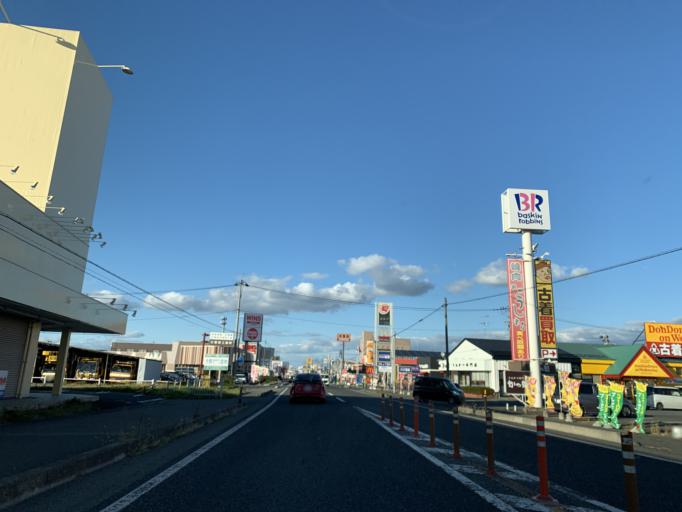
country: JP
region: Iwate
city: Mizusawa
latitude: 39.1455
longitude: 141.1497
